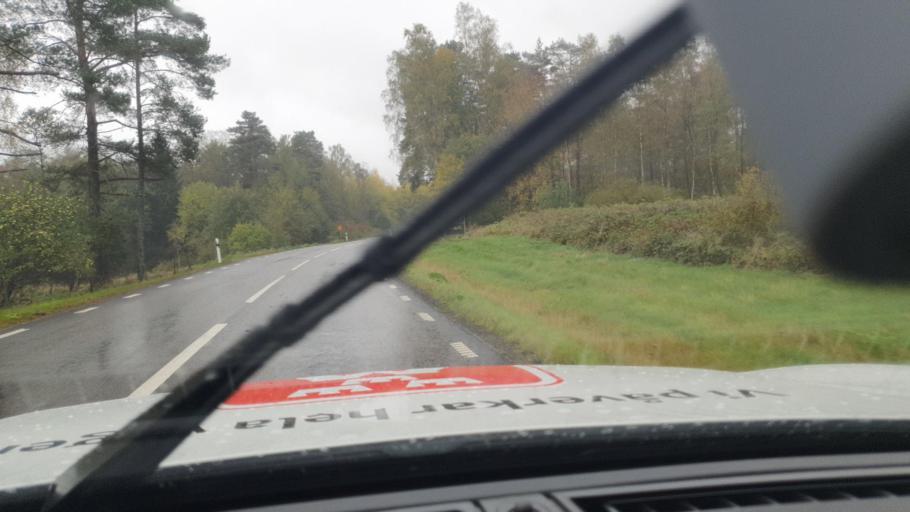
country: SE
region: Halland
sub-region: Halmstads Kommun
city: Getinge
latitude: 57.1467
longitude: 12.7280
